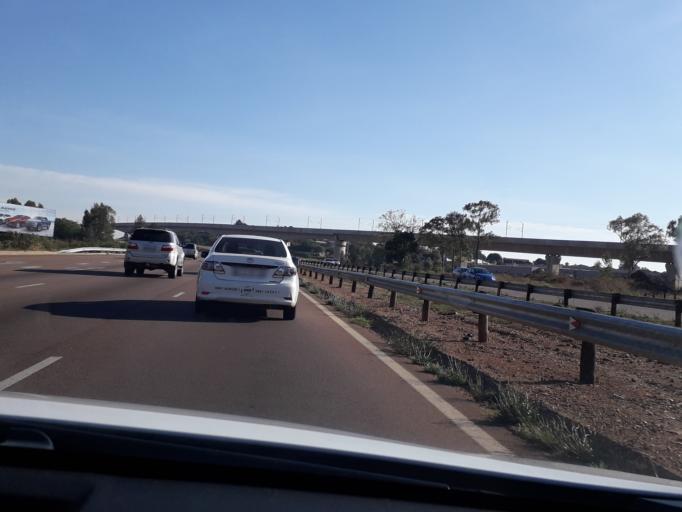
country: ZA
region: Gauteng
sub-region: City of Tshwane Metropolitan Municipality
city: Centurion
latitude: -25.8432
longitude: 28.1825
